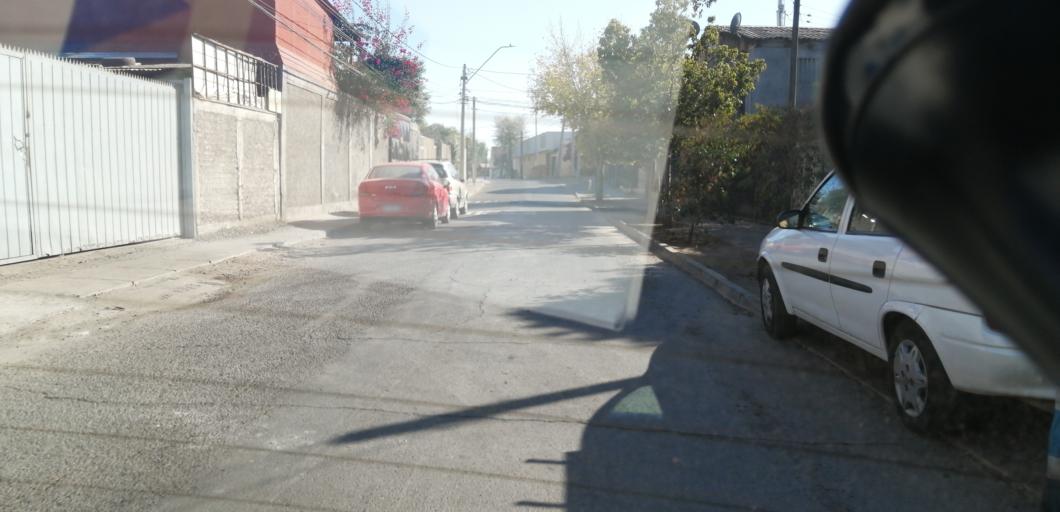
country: CL
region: Santiago Metropolitan
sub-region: Provincia de Santiago
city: Lo Prado
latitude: -33.4403
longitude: -70.7618
